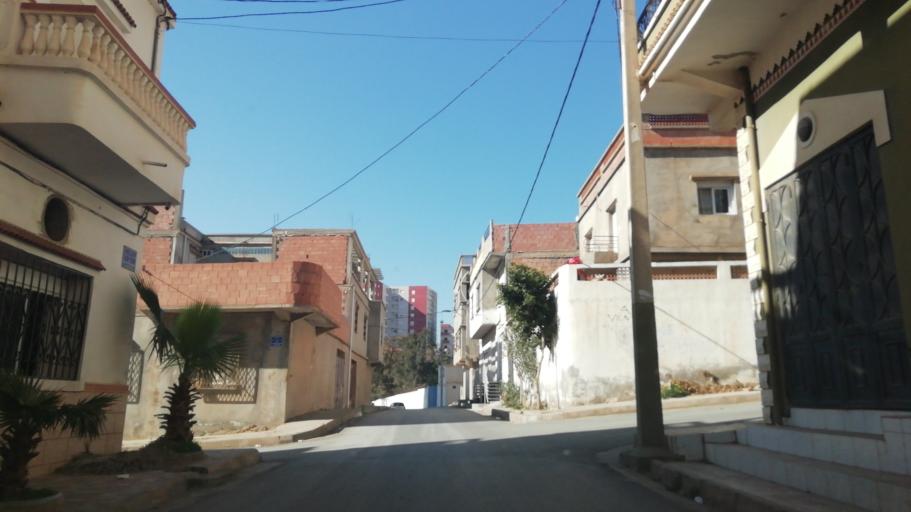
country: DZ
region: Oran
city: Bir el Djir
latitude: 35.7220
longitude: -0.5808
